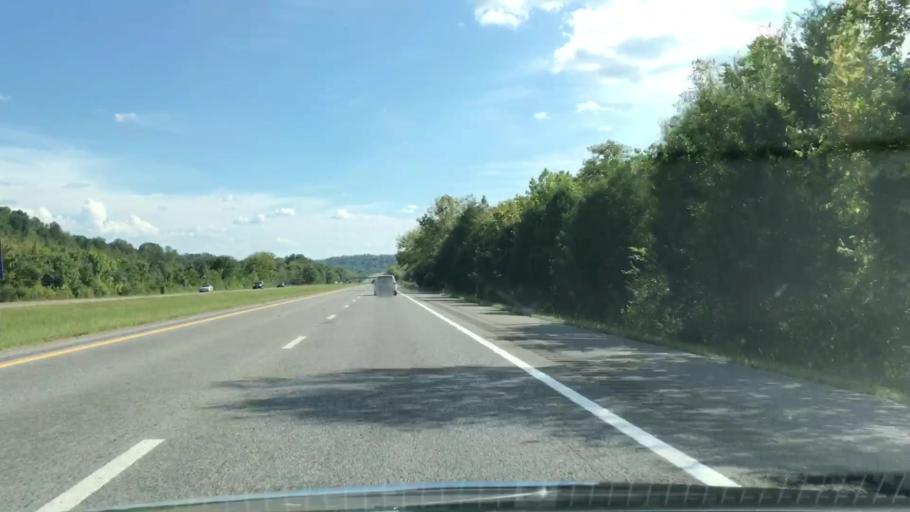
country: US
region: Alabama
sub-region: Limestone County
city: Ardmore
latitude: 35.1485
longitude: -86.8792
